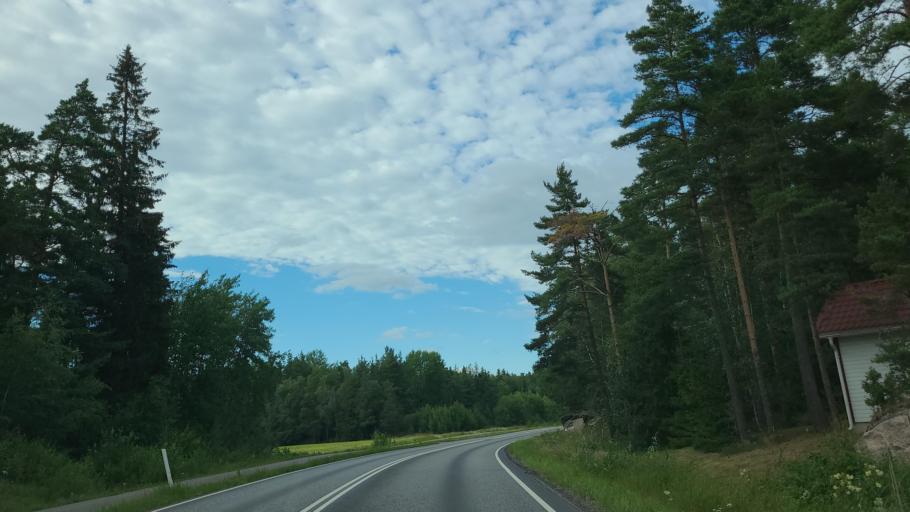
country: FI
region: Varsinais-Suomi
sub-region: Turku
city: Rymaettylae
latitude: 60.4073
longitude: 21.8949
